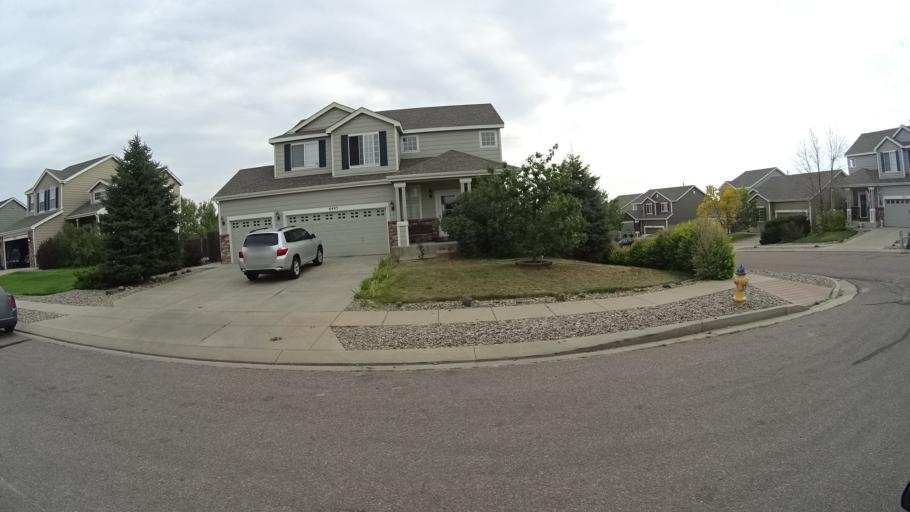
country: US
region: Colorado
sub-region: El Paso County
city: Cimarron Hills
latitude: 38.9232
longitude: -104.7079
